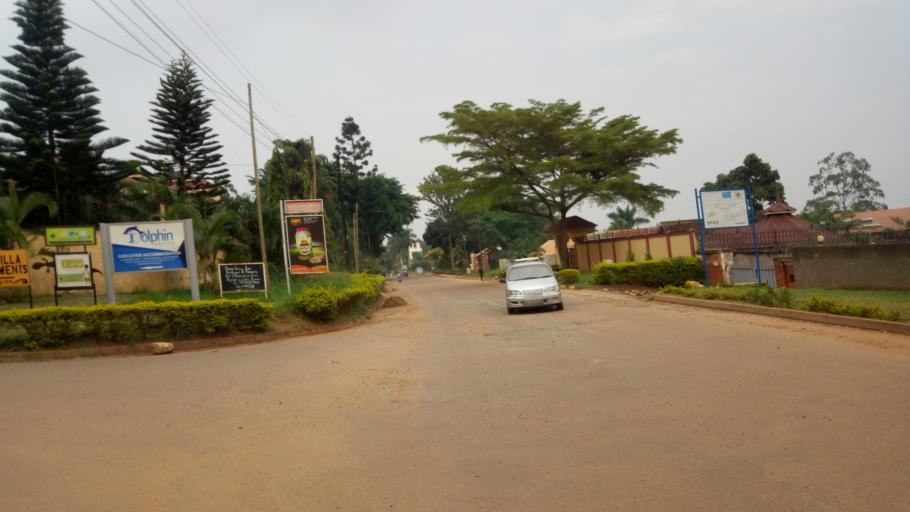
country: UG
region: Central Region
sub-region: Kampala District
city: Kampala
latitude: 0.3089
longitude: 32.6215
